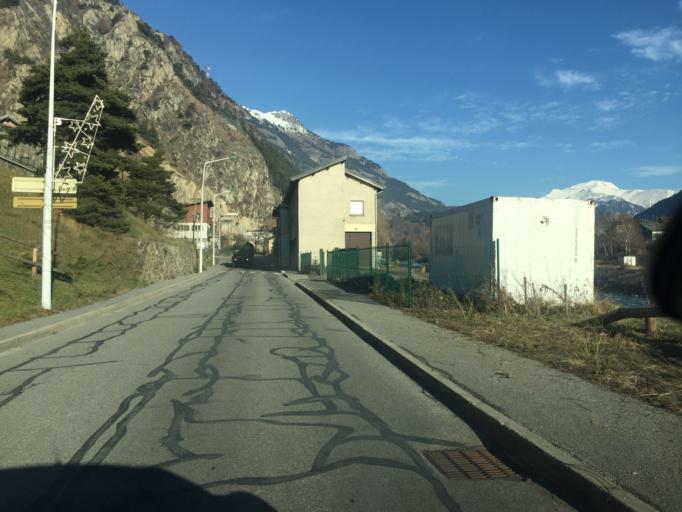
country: FR
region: Rhone-Alpes
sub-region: Departement de la Savoie
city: Modane
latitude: 45.2039
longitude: 6.6712
